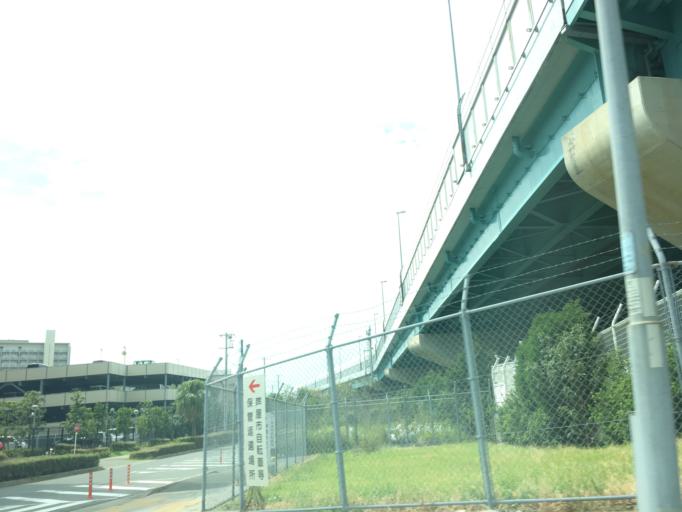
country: JP
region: Hyogo
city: Nishinomiya-hama
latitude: 34.7150
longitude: 135.3212
